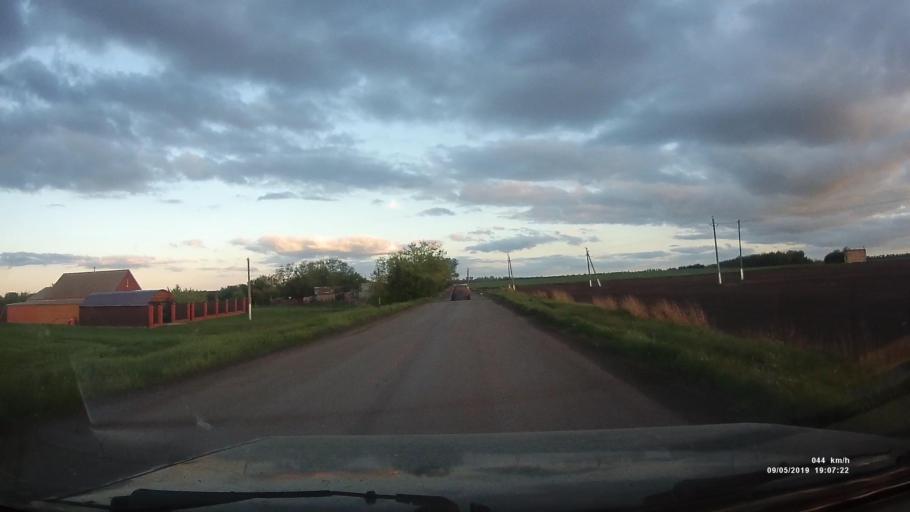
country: RU
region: Krasnodarskiy
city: Kanelovskaya
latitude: 46.7346
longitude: 39.1974
